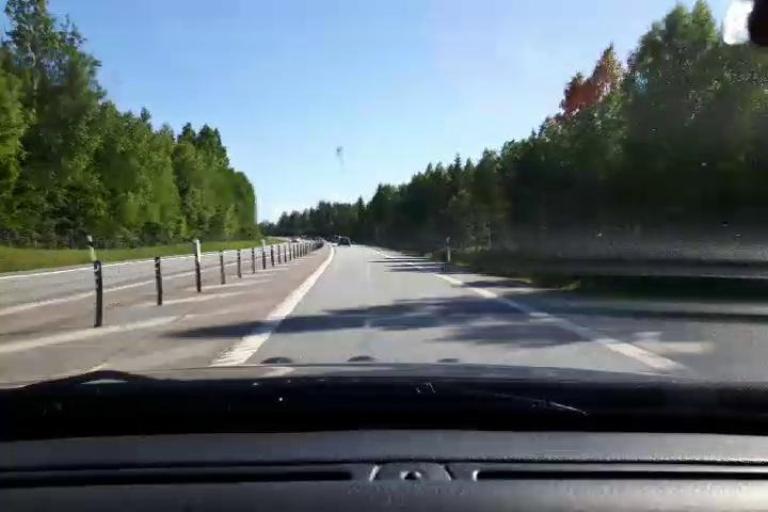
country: SE
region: Gaevleborg
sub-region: Gavle Kommun
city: Gavle
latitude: 60.7302
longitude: 17.0744
